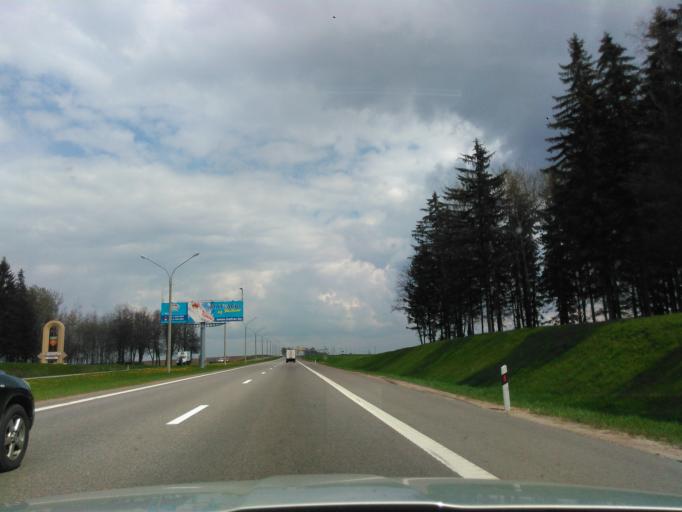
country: BY
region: Minsk
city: Slabada
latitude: 54.0057
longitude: 27.8461
